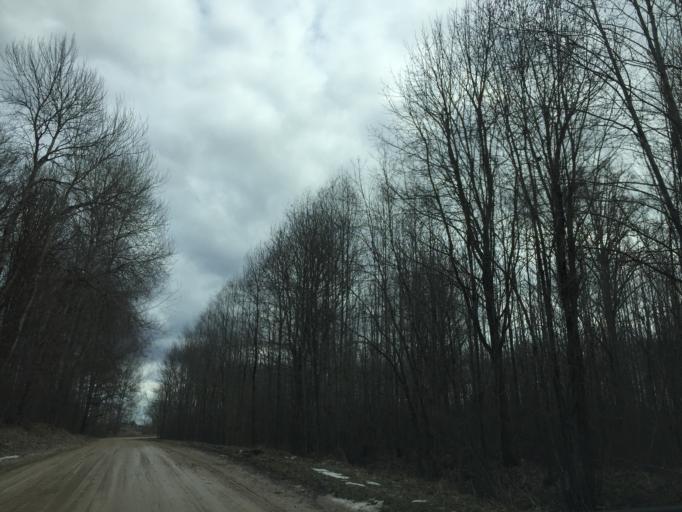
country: LV
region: Vecumnieki
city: Vecumnieki
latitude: 56.5026
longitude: 24.7191
